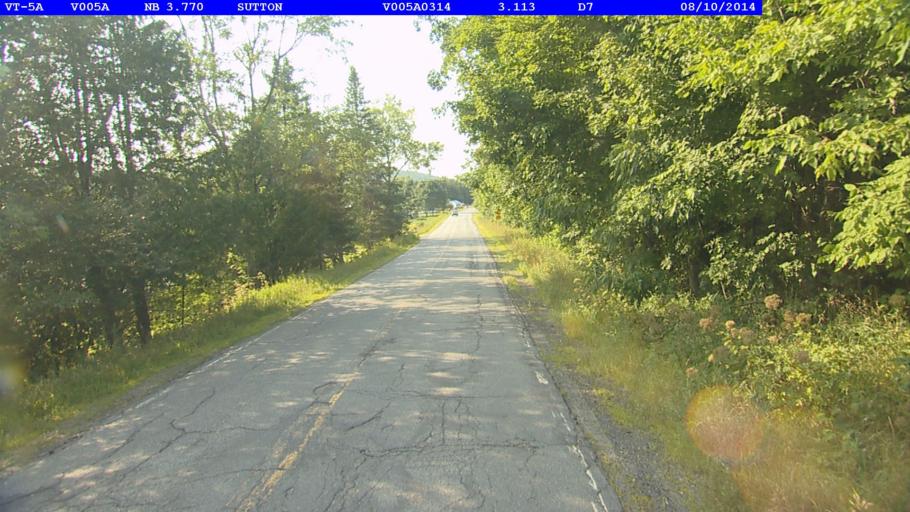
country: US
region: Vermont
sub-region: Caledonia County
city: Lyndonville
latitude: 44.6915
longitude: -71.9982
